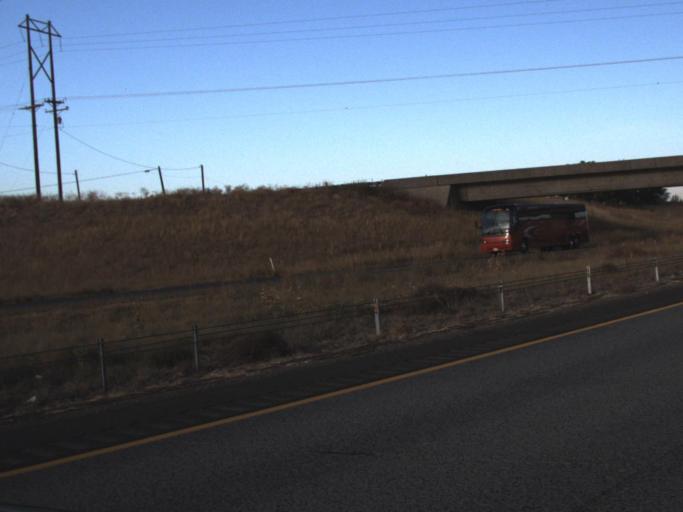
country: US
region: Washington
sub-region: Yakima County
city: Grandview
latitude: 46.2664
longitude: -119.9041
